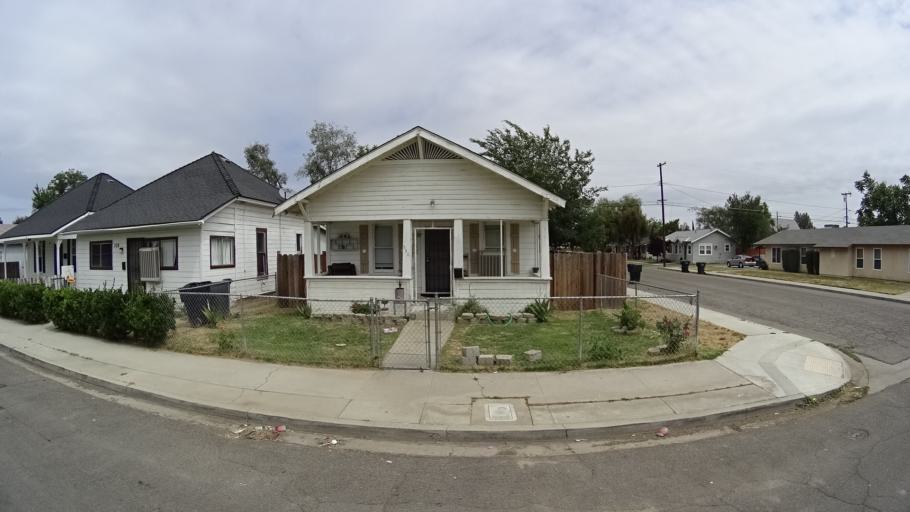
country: US
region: California
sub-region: Kings County
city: Hanford
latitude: 36.3291
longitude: -119.6413
